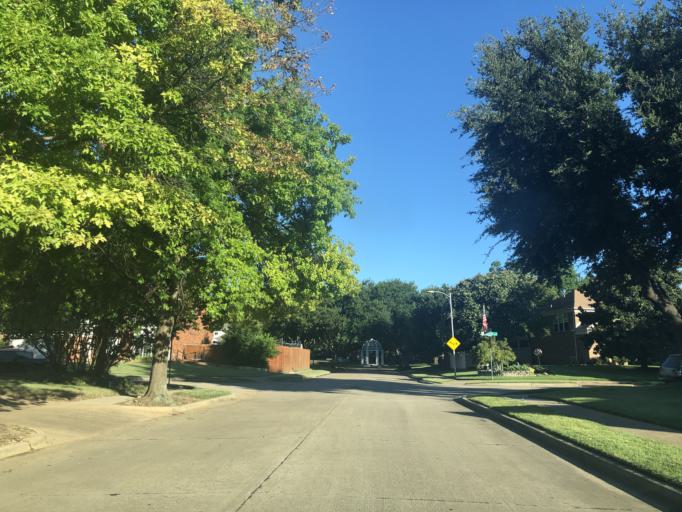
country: US
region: Texas
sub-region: Dallas County
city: Grand Prairie
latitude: 32.6655
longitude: -96.9962
